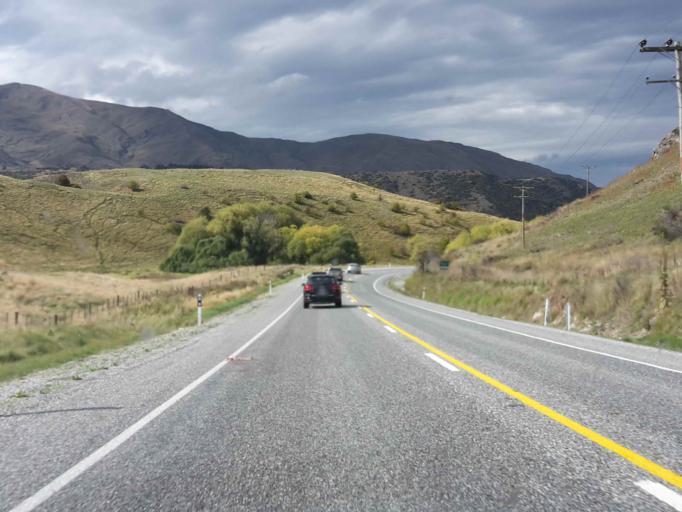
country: NZ
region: Otago
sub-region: Queenstown-Lakes District
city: Arrowtown
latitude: -44.9791
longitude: 168.8306
